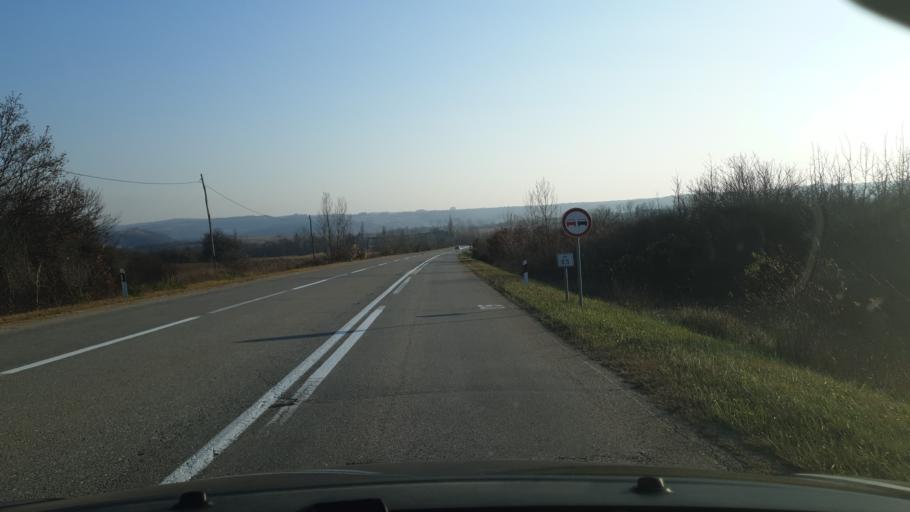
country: RS
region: Central Serbia
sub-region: Zajecarski Okrug
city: Zajecar
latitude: 44.1044
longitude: 22.3475
